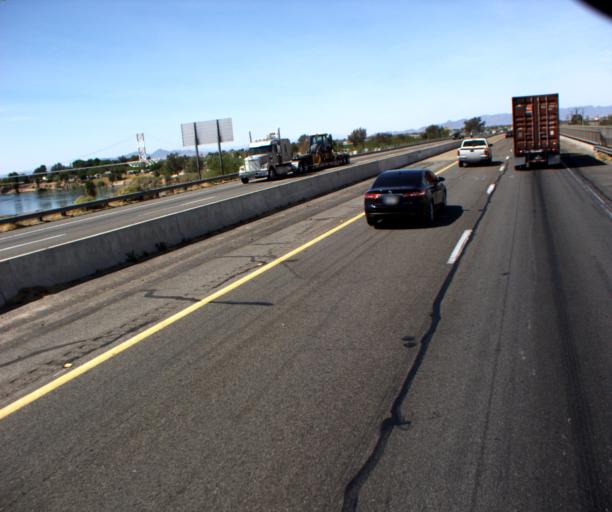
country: US
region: Arizona
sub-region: La Paz County
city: Ehrenberg
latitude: 33.6043
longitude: -114.5287
